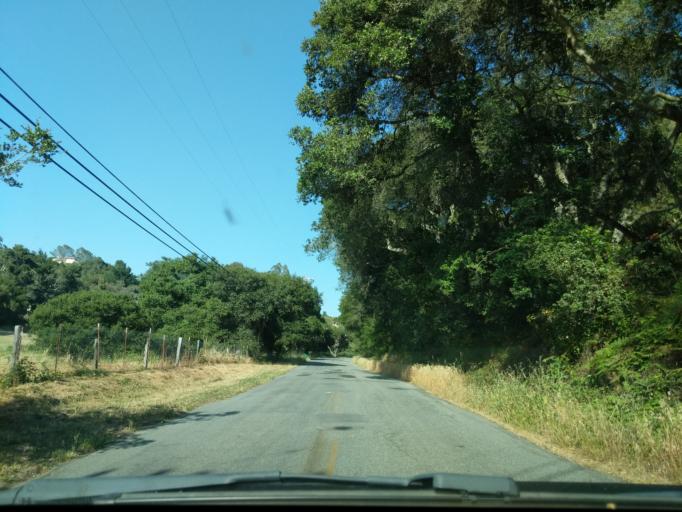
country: US
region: California
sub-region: Monterey County
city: Prunedale
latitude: 36.8021
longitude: -121.6387
